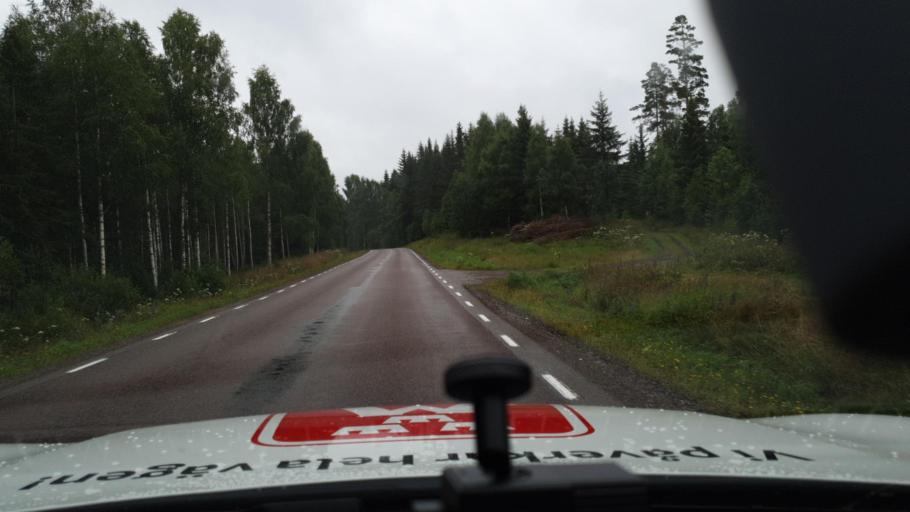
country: SE
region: Vaermland
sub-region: Torsby Kommun
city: Torsby
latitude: 59.9393
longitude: 12.7471
